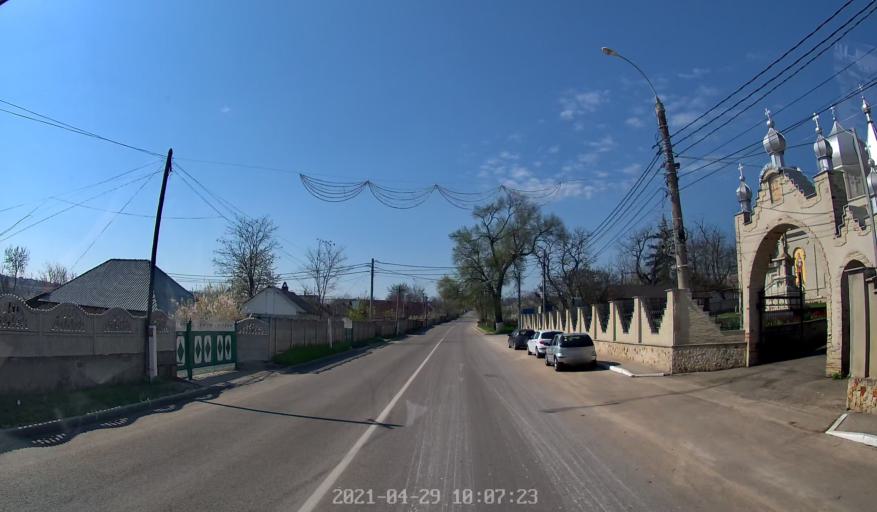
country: MD
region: Chisinau
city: Cricova
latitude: 47.1357
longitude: 28.8669
